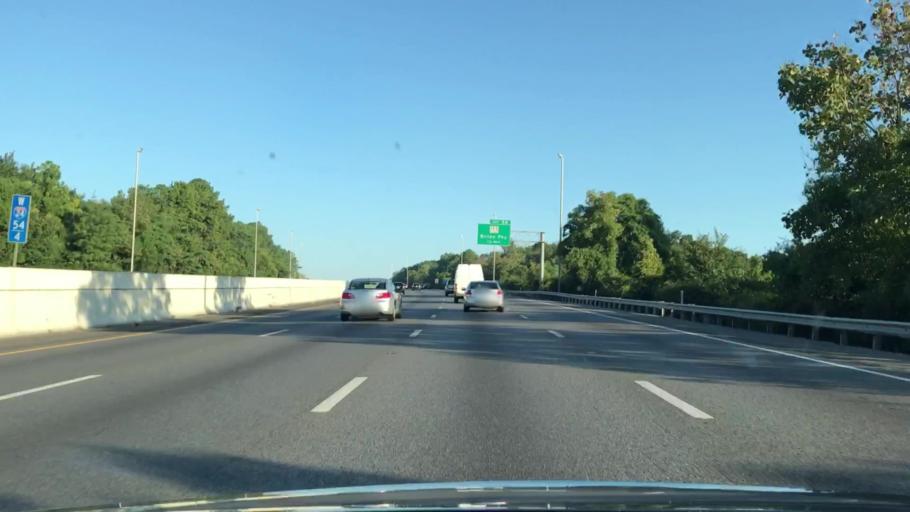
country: US
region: Tennessee
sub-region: Davidson County
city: Oak Hill
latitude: 36.1168
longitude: -86.7313
